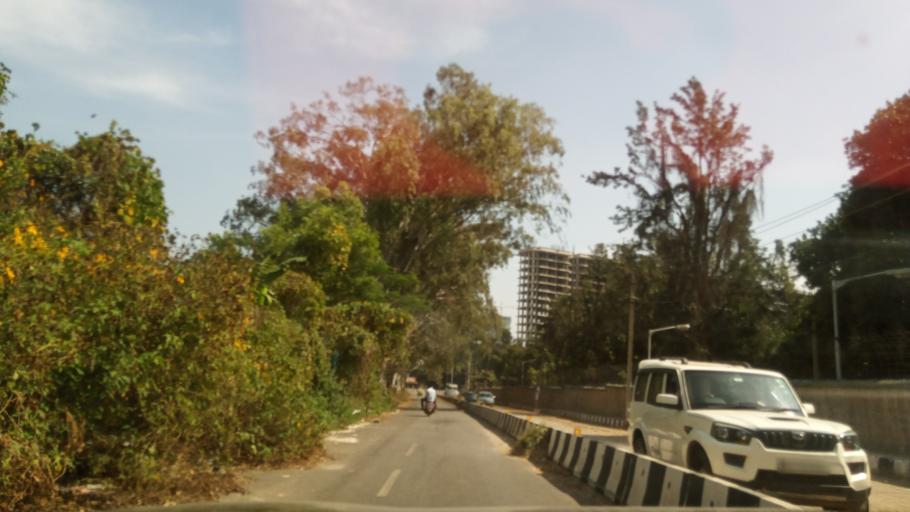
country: IN
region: Karnataka
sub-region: Bangalore Urban
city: Bangalore
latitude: 13.0338
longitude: 77.5390
